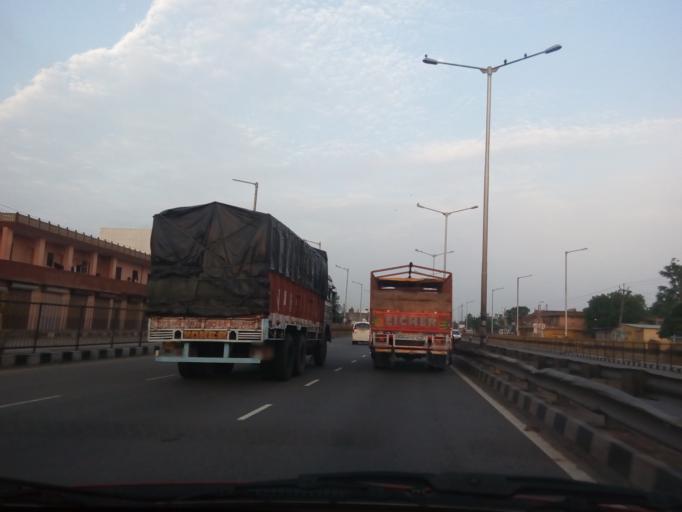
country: IN
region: Rajasthan
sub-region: Jaipur
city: Jaipur
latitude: 26.8745
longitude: 75.7075
